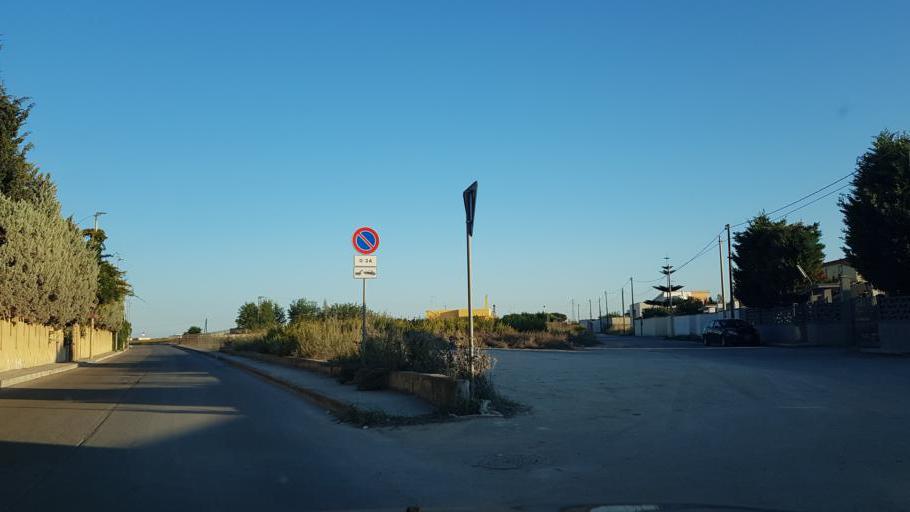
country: IT
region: Apulia
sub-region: Provincia di Brindisi
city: Brindisi
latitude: 40.6177
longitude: 17.9160
